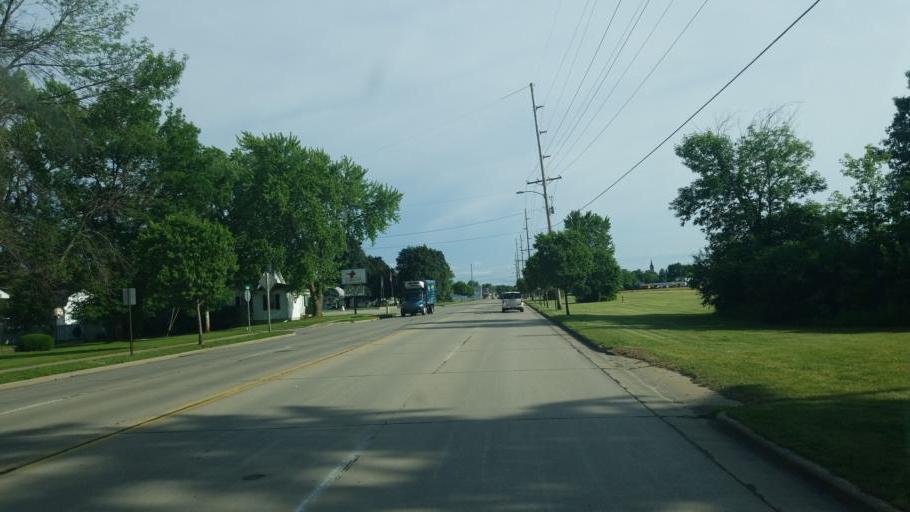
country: US
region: Wisconsin
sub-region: Monroe County
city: Tomah
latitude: 43.9906
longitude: -90.5047
